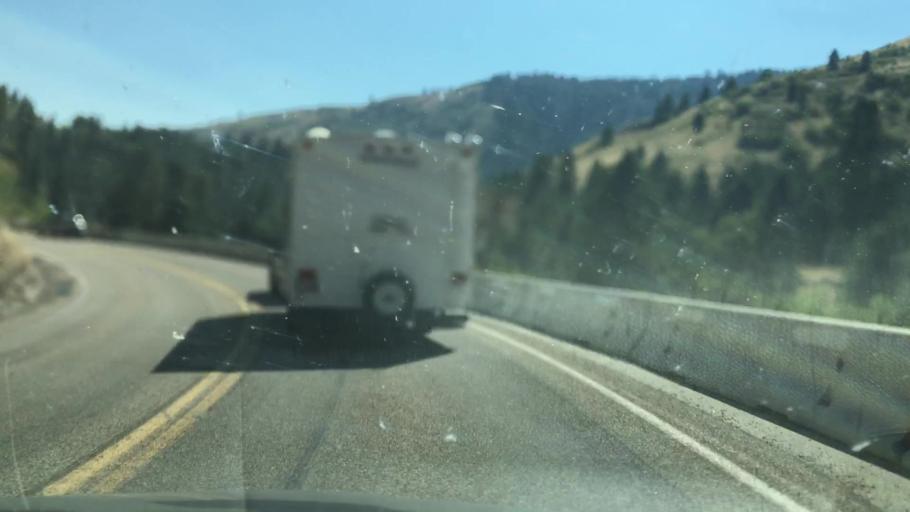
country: US
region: Idaho
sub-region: Boise County
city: Idaho City
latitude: 44.0894
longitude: -116.1113
